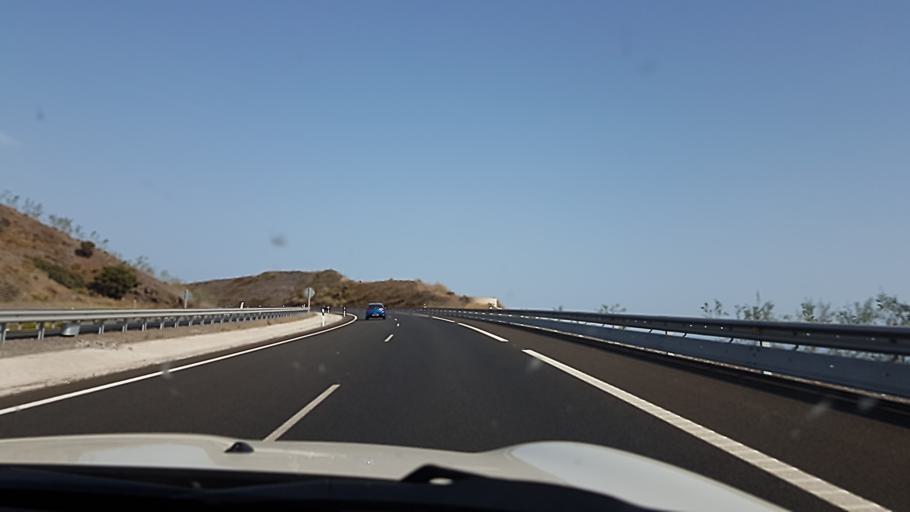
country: ES
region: Andalusia
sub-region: Provincia de Granada
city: Albunol
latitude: 36.7512
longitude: -3.2153
